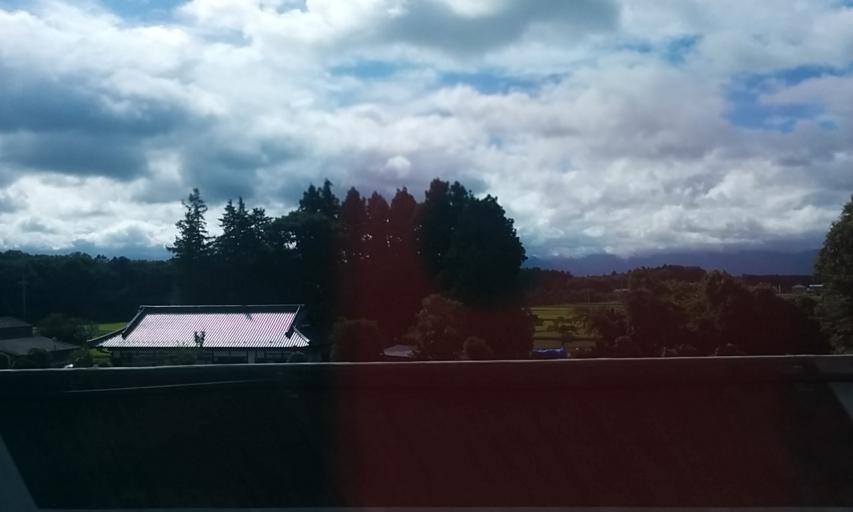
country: JP
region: Tochigi
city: Otawara
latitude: 36.9152
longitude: 140.0086
